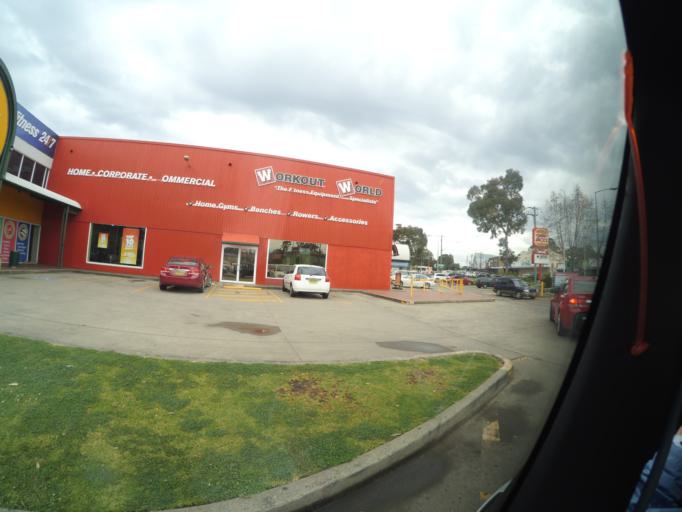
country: AU
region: New South Wales
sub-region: Bankstown
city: Bankstown
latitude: -33.9328
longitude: 151.0282
